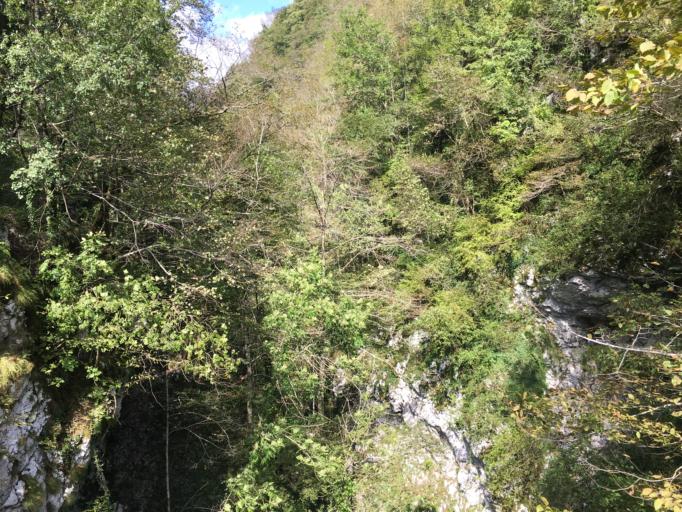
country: SI
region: Tolmin
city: Tolmin
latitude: 46.2014
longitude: 13.7420
